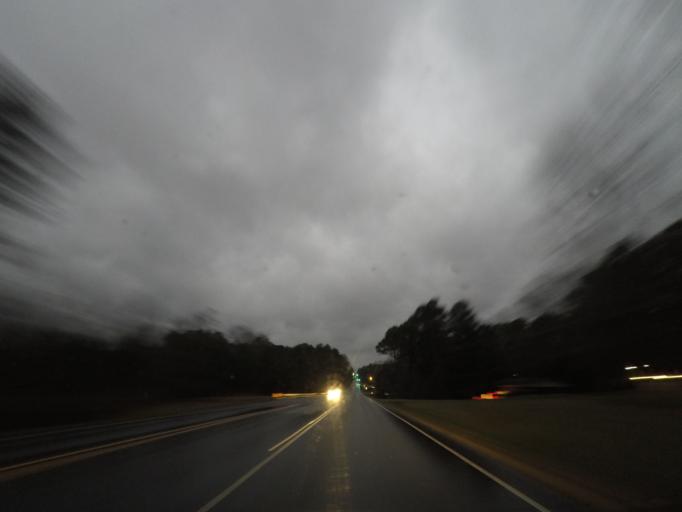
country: US
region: North Carolina
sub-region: Orange County
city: Hillsborough
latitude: 36.0844
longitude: -79.0872
